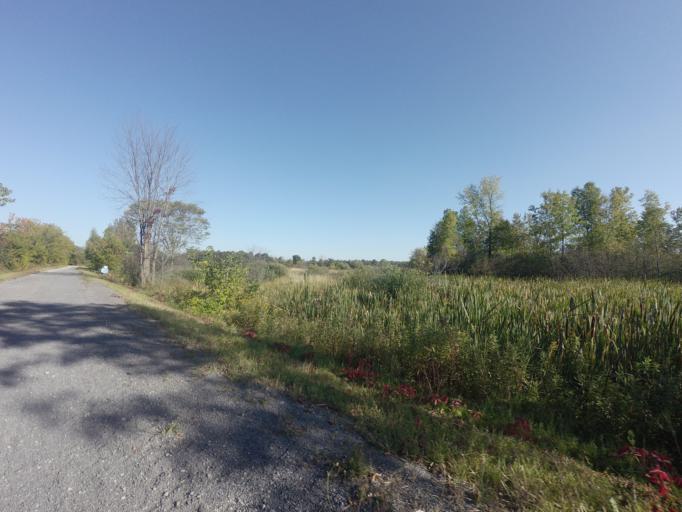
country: CA
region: Ontario
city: Hawkesbury
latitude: 45.5373
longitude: -74.6262
